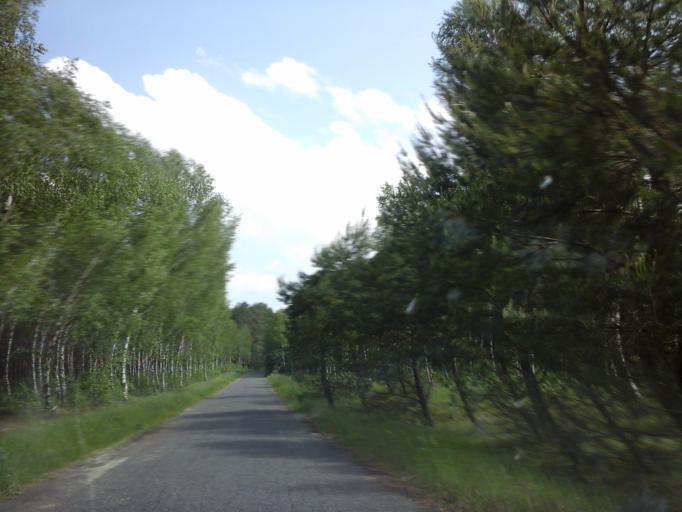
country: PL
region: West Pomeranian Voivodeship
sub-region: Powiat choszczenski
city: Drawno
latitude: 53.1864
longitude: 15.8689
